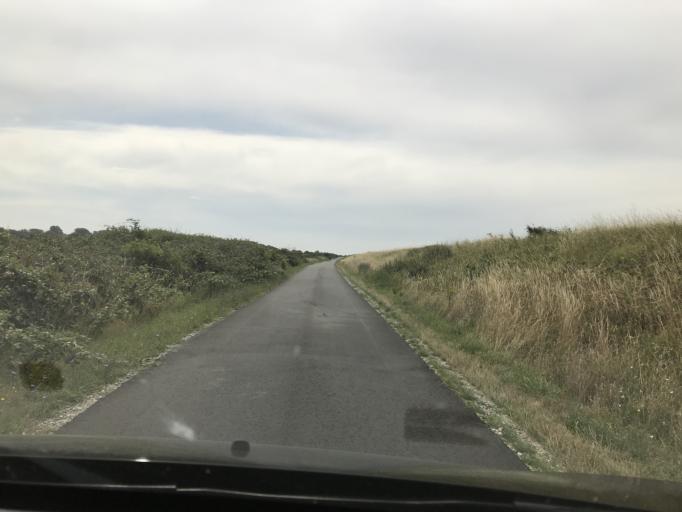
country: DK
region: South Denmark
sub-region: Faaborg-Midtfyn Kommune
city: Faaborg
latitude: 54.9287
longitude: 10.2451
